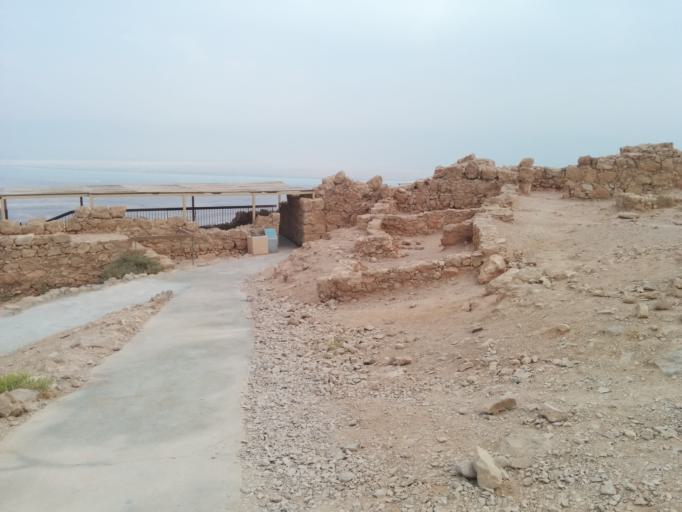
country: IL
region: Southern District
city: `En Boqeq
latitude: 31.3145
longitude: 35.3546
